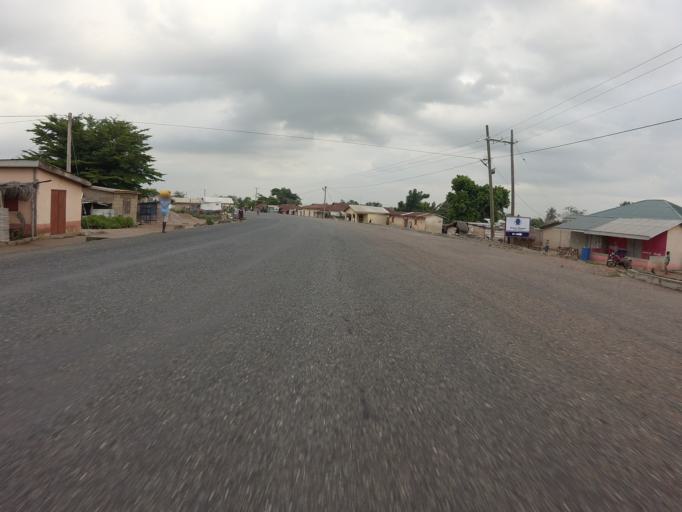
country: GH
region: Volta
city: Ho
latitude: 6.4890
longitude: 0.4881
